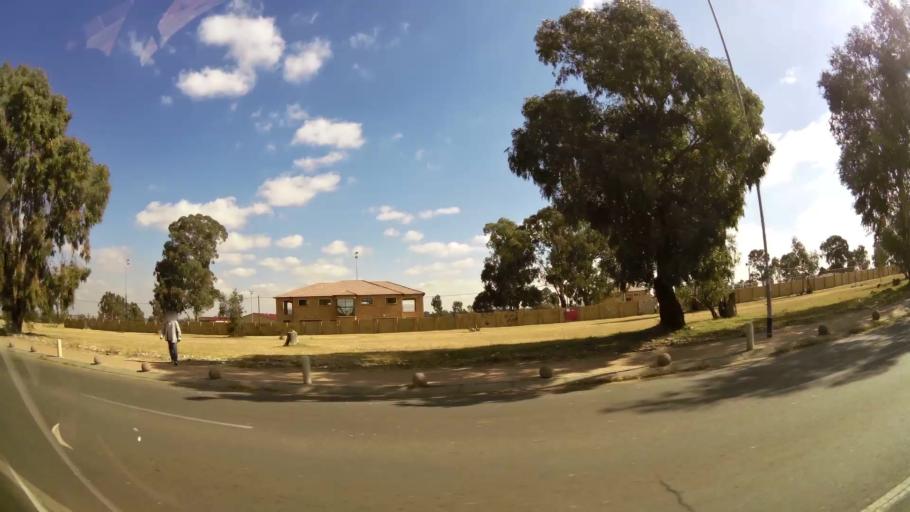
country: ZA
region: Gauteng
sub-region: West Rand District Municipality
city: Krugersdorp
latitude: -26.1482
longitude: 27.7892
